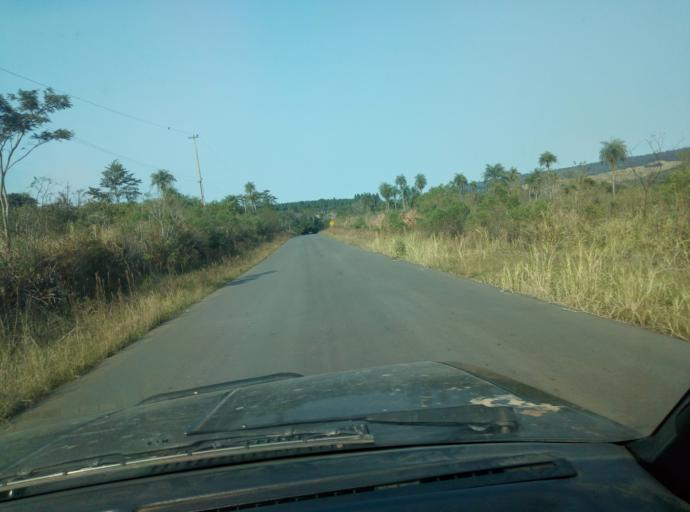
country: PY
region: Caaguazu
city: Carayao
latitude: -25.2387
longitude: -56.2869
